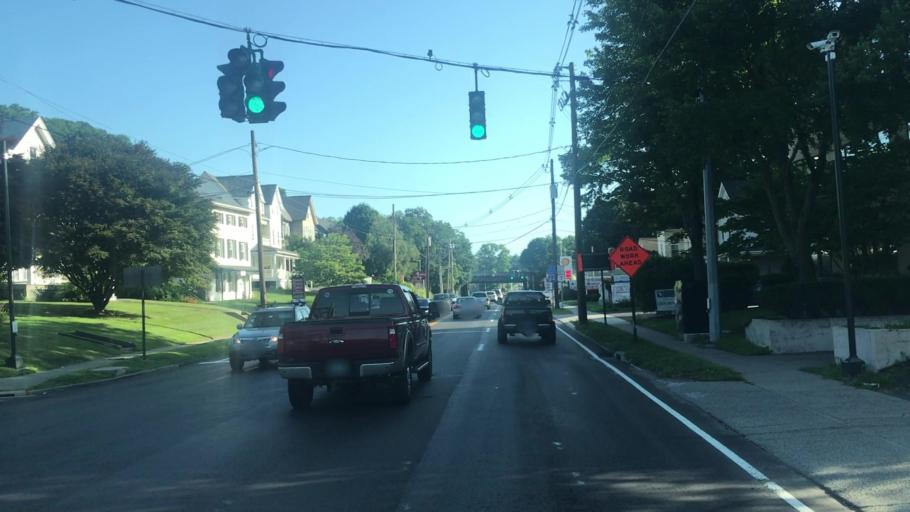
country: US
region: Connecticut
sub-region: Fairfield County
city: Danbury
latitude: 41.4072
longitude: -73.4560
